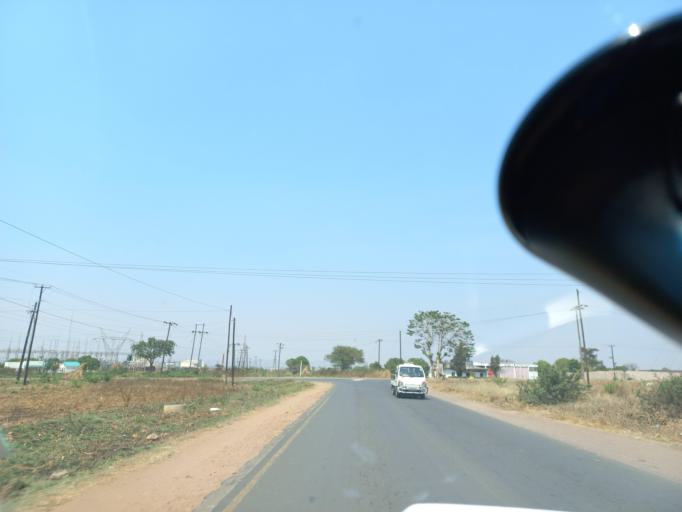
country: ZM
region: Lusaka
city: Kafue
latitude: -15.7500
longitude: 28.1629
